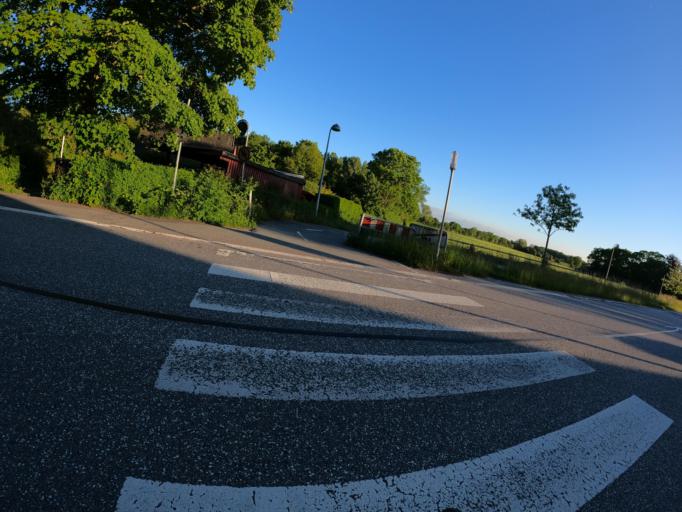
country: DK
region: Capital Region
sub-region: Hoje-Taastrup Kommune
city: Taastrup
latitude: 55.6290
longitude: 12.2788
